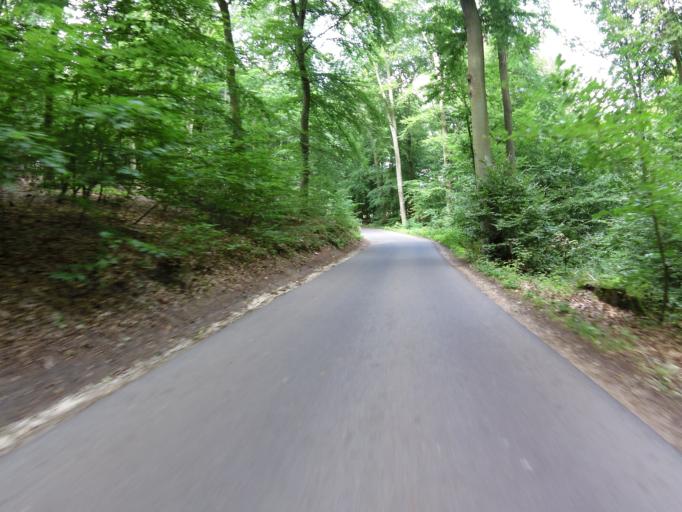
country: DE
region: Mecklenburg-Vorpommern
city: Seebad Bansin
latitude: 53.9586
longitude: 14.1063
